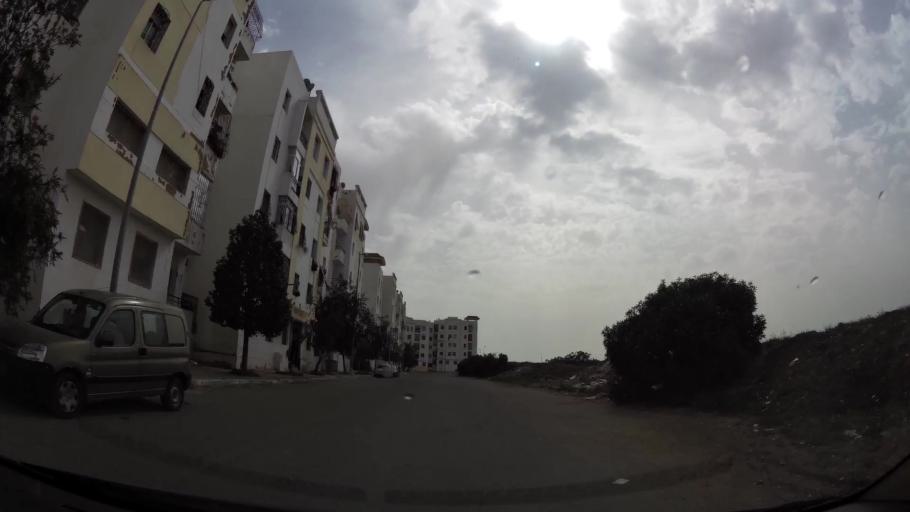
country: MA
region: Tanger-Tetouan
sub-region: Tanger-Assilah
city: Boukhalef
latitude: 35.7402
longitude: -5.8896
